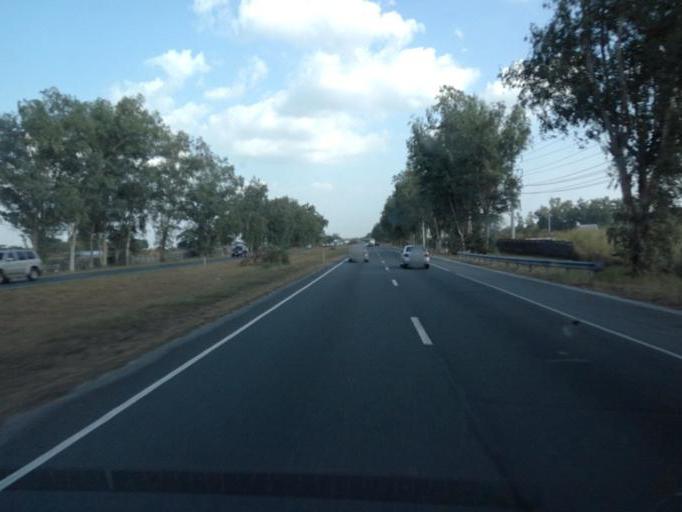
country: PH
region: Central Luzon
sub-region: Province of Pampanga
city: Culubasa
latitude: 15.1442
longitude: 120.6286
